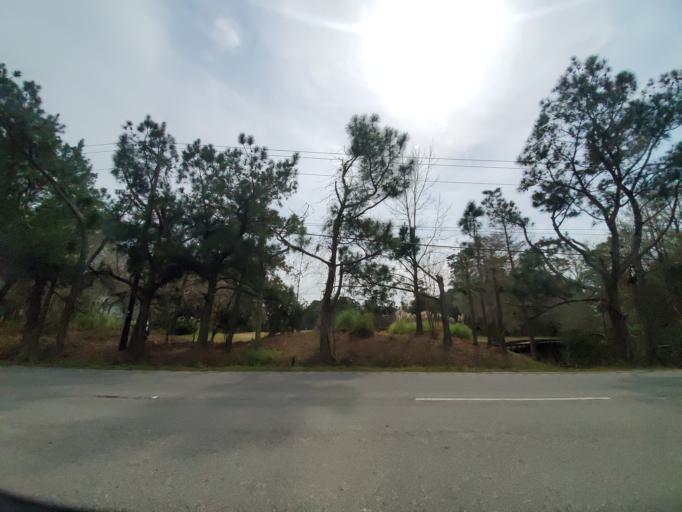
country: US
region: South Carolina
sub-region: Dorchester County
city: Centerville
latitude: 32.9488
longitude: -80.2276
